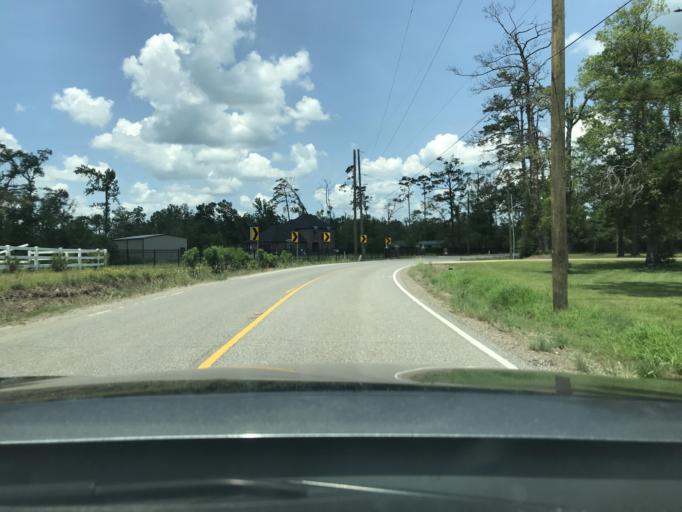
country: US
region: Louisiana
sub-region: Calcasieu Parish
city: Moss Bluff
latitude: 30.3250
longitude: -93.1742
